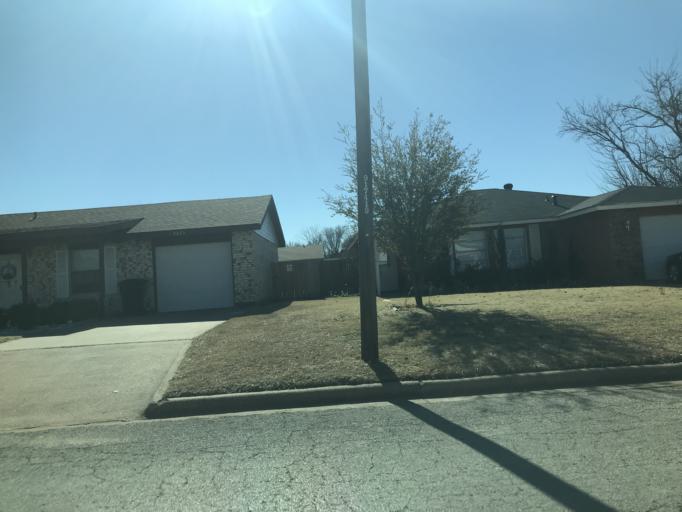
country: US
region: Texas
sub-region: Taylor County
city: Abilene
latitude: 32.4399
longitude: -99.7894
